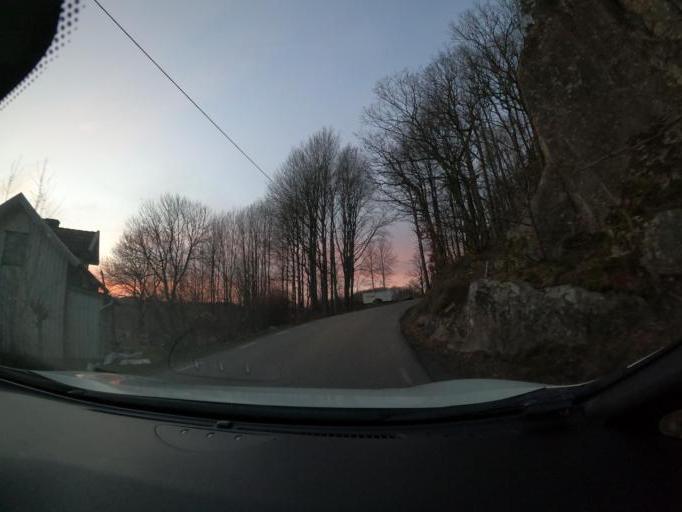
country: SE
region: Vaestra Goetaland
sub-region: Harryda Kommun
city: Molnlycke
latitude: 57.6063
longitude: 12.1559
